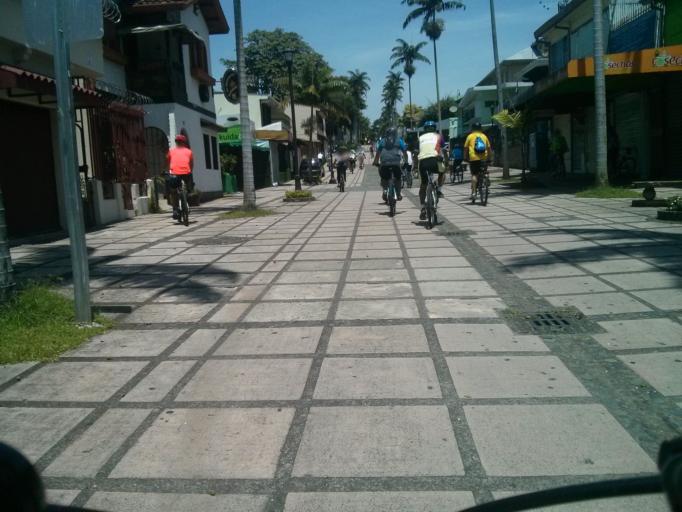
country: CR
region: San Jose
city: San Jose
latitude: 9.9311
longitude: -84.0712
